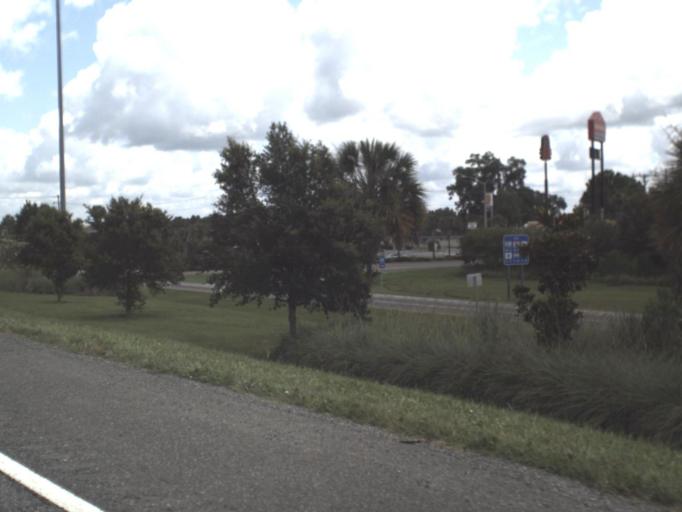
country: US
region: Florida
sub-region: Columbia County
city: Lake City
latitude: 30.1787
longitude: -82.6879
